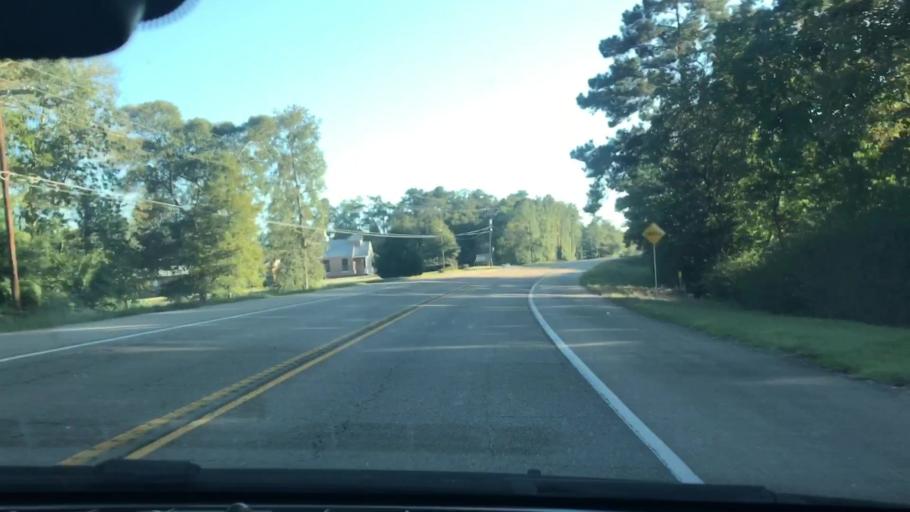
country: US
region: Louisiana
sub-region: Washington Parish
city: Bogalusa
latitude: 30.5953
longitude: -89.8714
